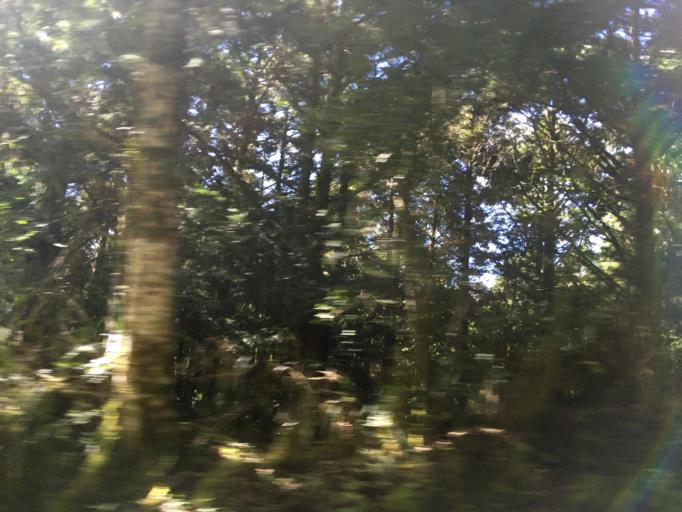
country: TW
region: Taiwan
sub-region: Yilan
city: Yilan
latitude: 24.5119
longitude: 121.5864
